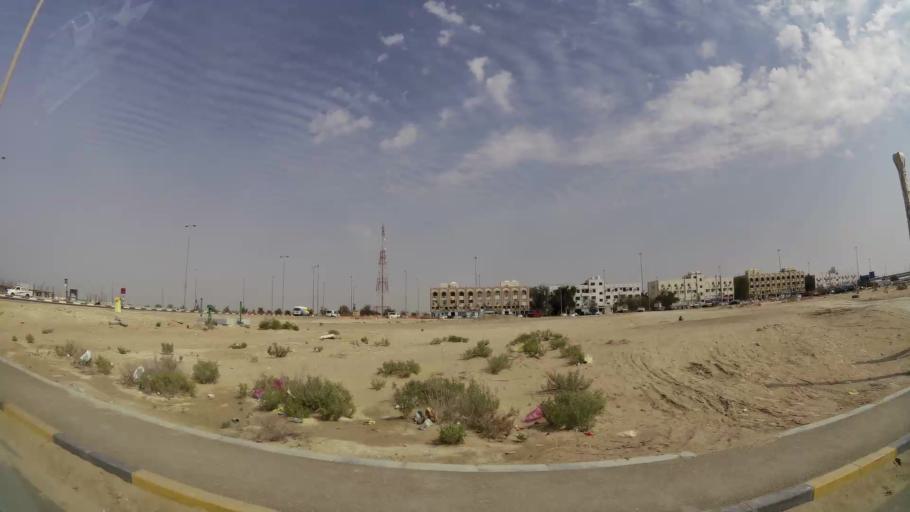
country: AE
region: Abu Dhabi
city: Abu Dhabi
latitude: 24.5603
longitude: 54.6927
